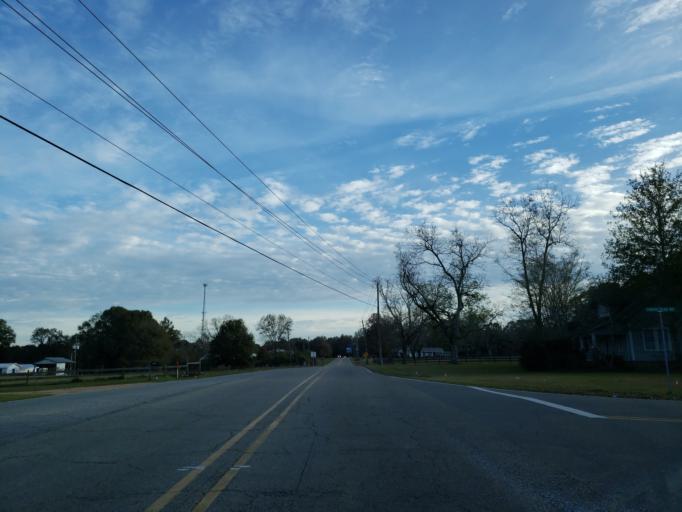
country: US
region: Mississippi
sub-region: Lamar County
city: Purvis
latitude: 31.1605
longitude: -89.4212
